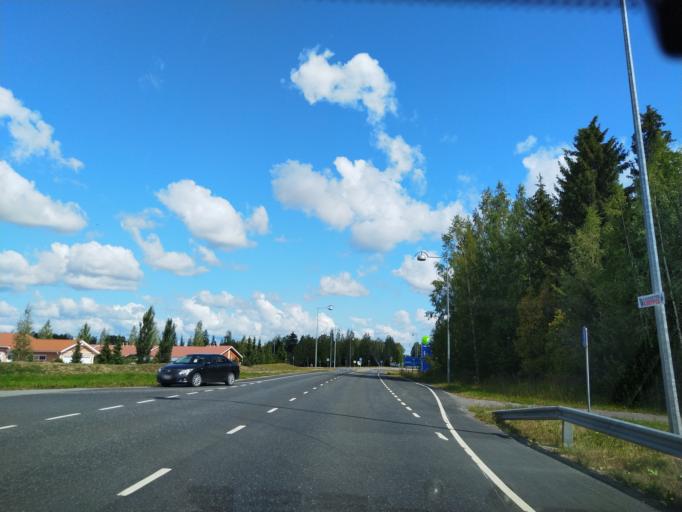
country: FI
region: Satakunta
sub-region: Pori
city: Huittinen
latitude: 61.1718
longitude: 22.7086
